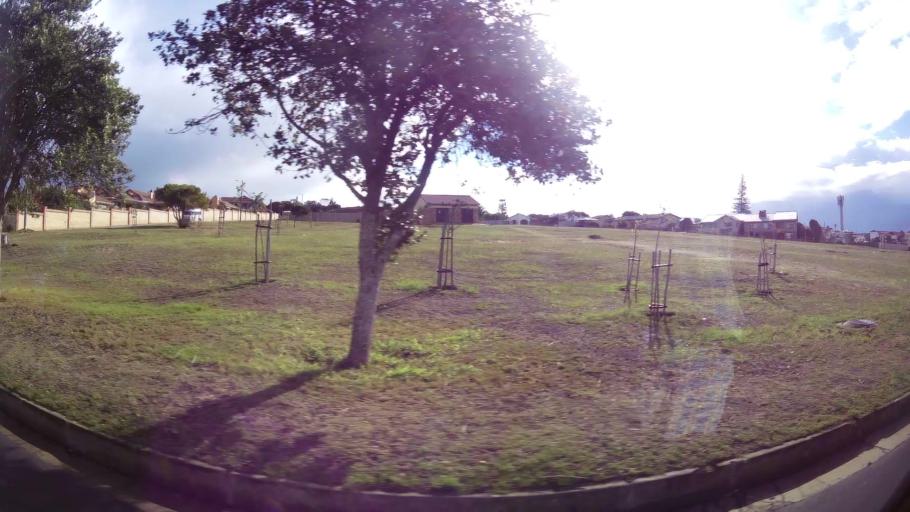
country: ZA
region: Western Cape
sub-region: Eden District Municipality
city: Mossel Bay
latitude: -34.1861
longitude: 22.1327
